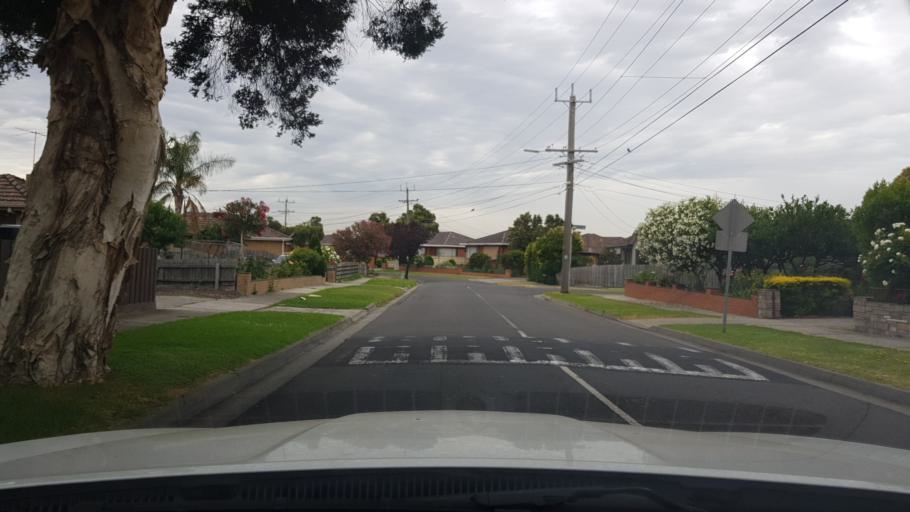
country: AU
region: Victoria
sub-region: Whittlesea
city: Lalor
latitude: -37.6620
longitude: 145.0136
